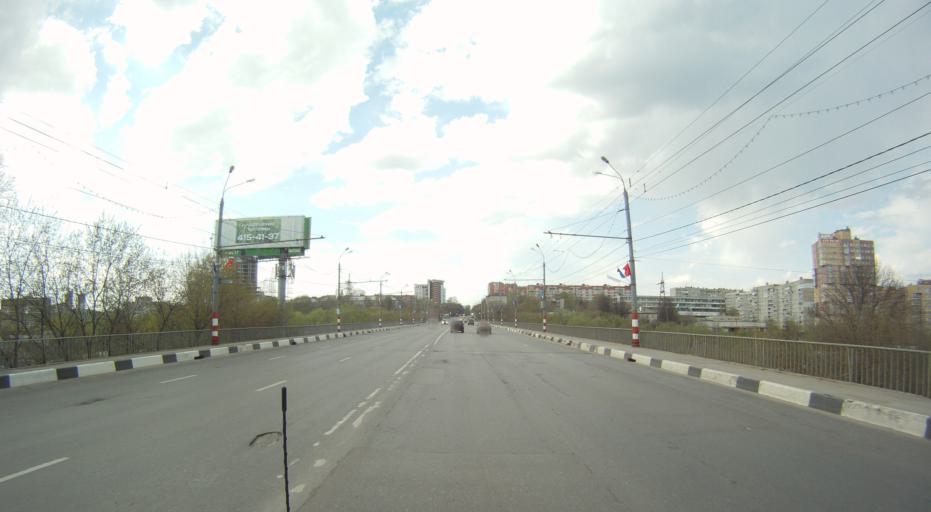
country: RU
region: Nizjnij Novgorod
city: Nizhniy Novgorod
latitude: 56.3048
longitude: 44.0269
